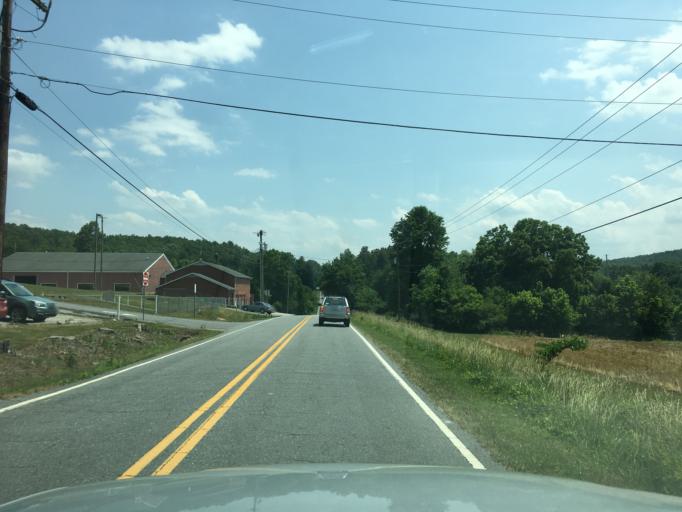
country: US
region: North Carolina
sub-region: McDowell County
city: West Marion
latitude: 35.6128
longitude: -81.9820
